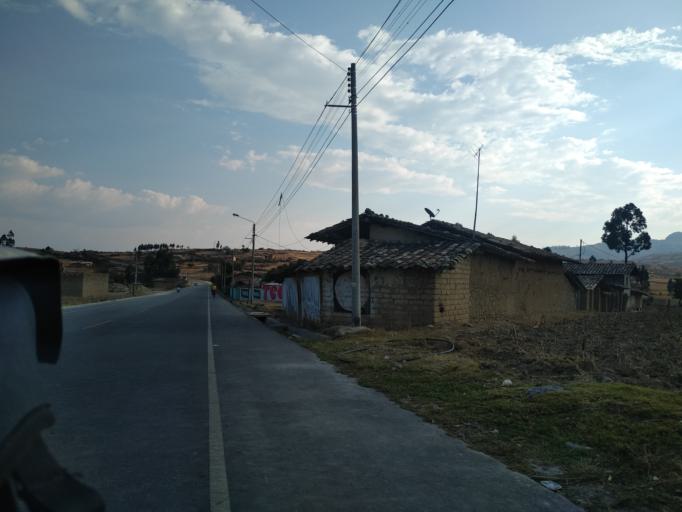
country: PE
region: Cajamarca
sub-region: San Marcos
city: La Grama
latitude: -7.3946
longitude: -78.1244
